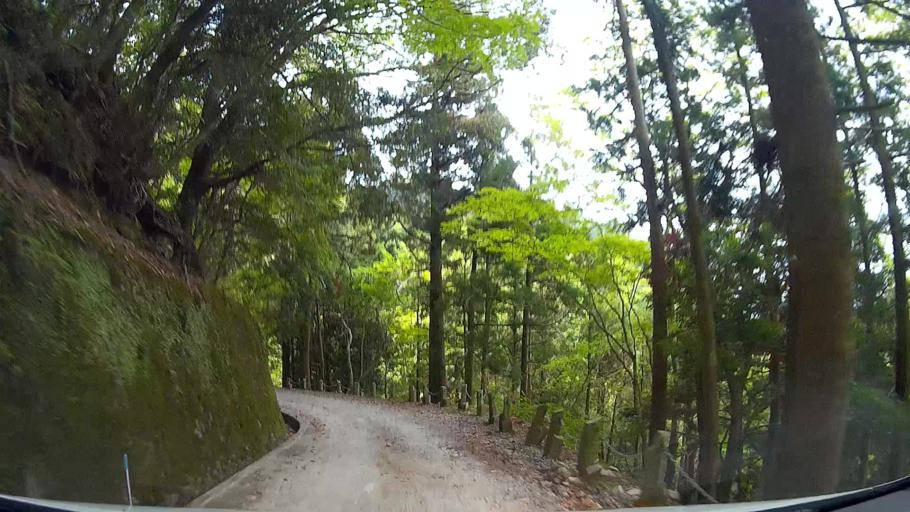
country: JP
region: Shizuoka
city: Shimoda
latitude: 34.8291
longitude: 138.9373
